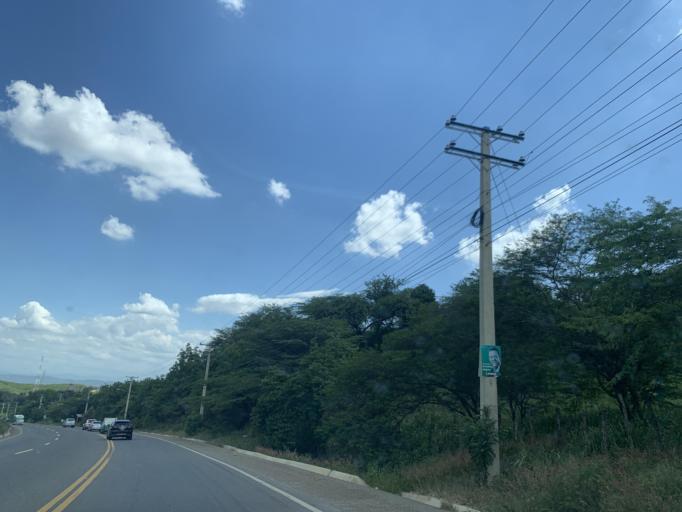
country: DO
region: Santiago
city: Villa Bisono
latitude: 19.5873
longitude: -70.8464
